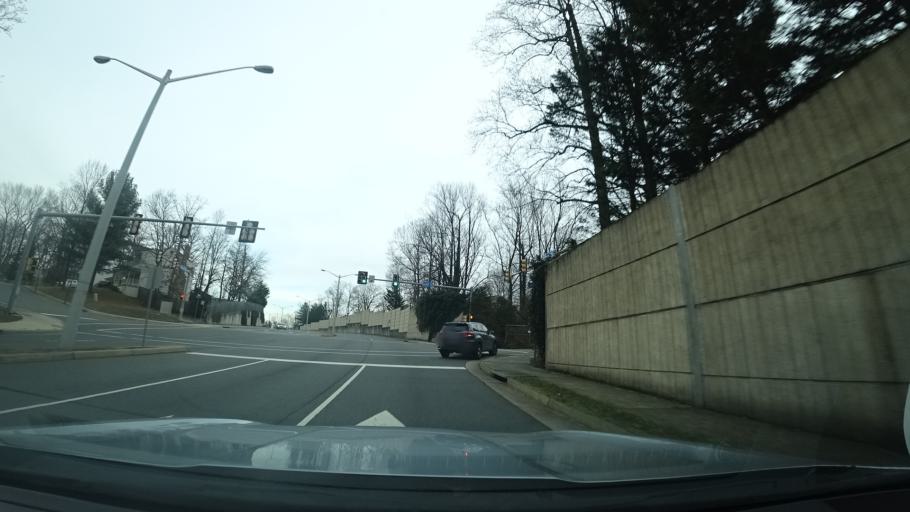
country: US
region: Virginia
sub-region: Fairfax County
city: Herndon
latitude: 38.9822
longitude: -77.3827
